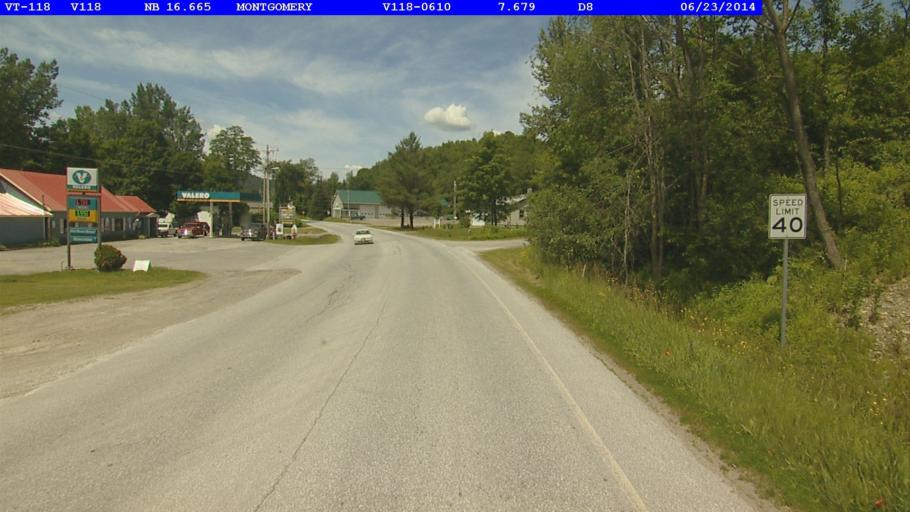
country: US
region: Vermont
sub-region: Franklin County
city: Richford
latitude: 44.9000
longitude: -72.6336
